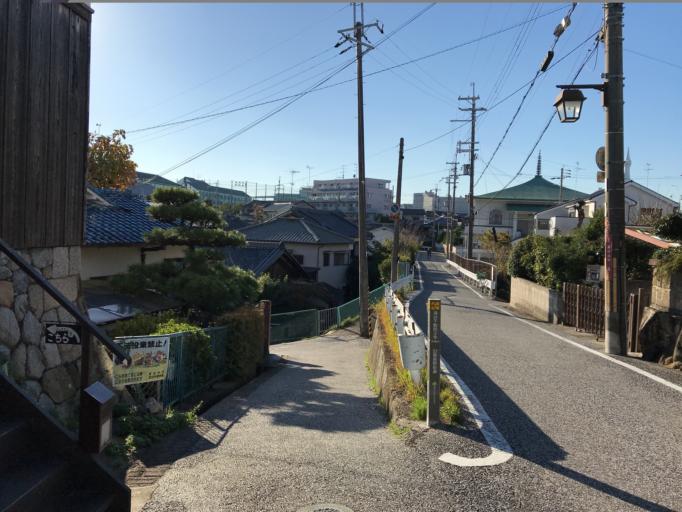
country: JP
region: Osaka
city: Tondabayashicho
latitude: 34.4989
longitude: 135.6017
